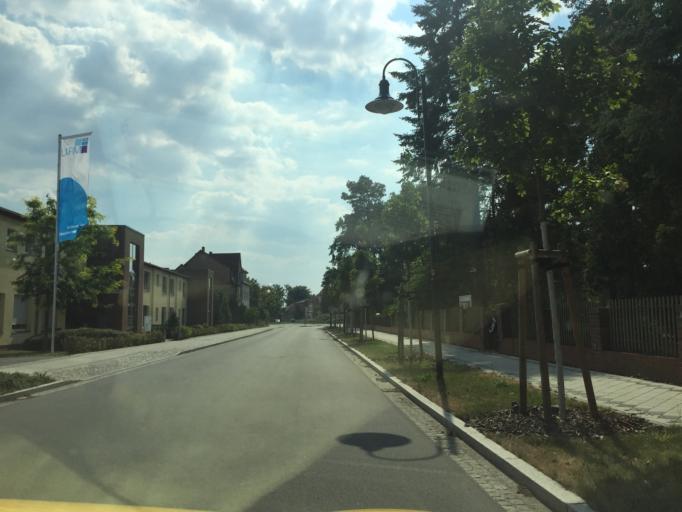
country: DE
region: Brandenburg
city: Welzow
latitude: 51.5780
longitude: 14.1735
